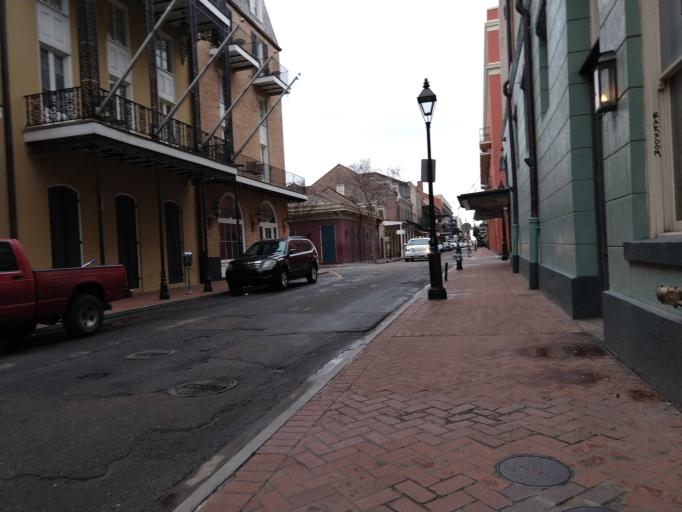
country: US
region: Louisiana
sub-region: Orleans Parish
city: New Orleans
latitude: 29.9563
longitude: -90.0696
